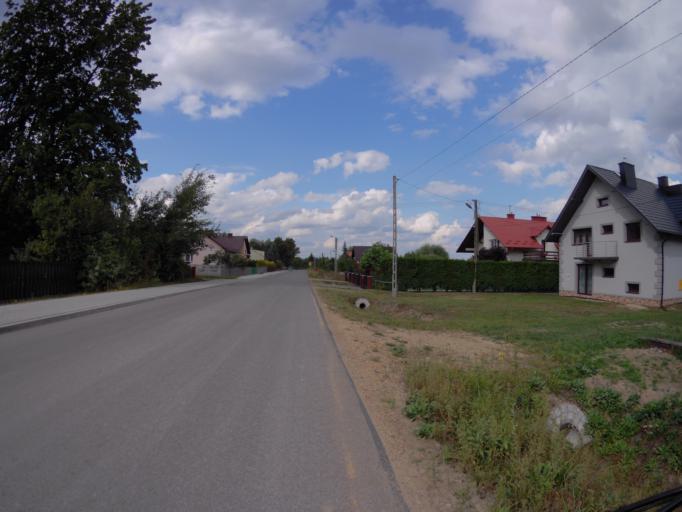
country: PL
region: Subcarpathian Voivodeship
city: Nowa Sarzyna
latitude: 50.2826
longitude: 22.3516
